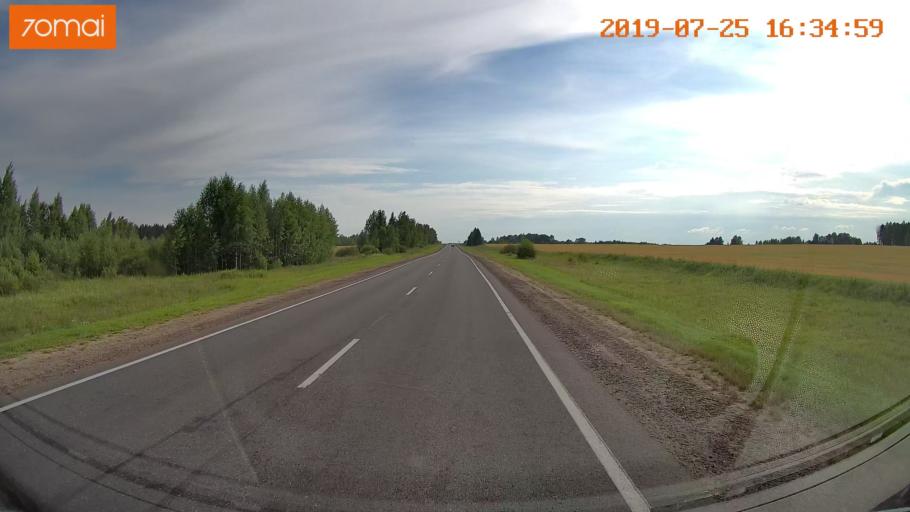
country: RU
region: Ivanovo
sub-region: Privolzhskiy Rayon
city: Ples
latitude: 57.4112
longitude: 41.4275
